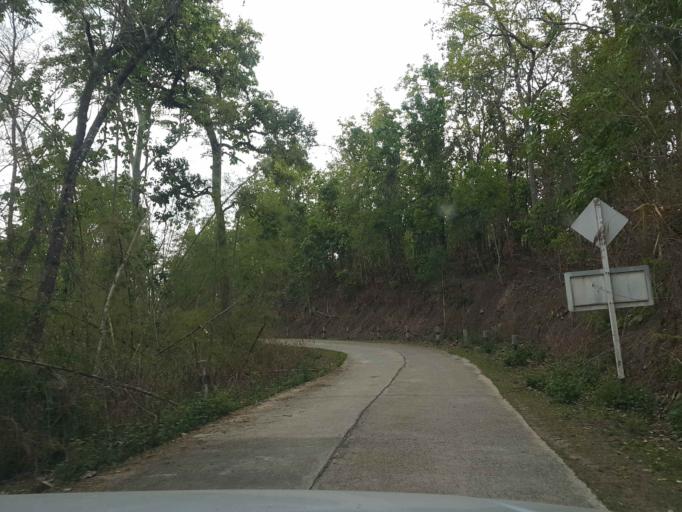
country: TH
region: Chiang Mai
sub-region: Amphoe Chiang Dao
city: Chiang Dao
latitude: 19.3851
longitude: 98.7729
